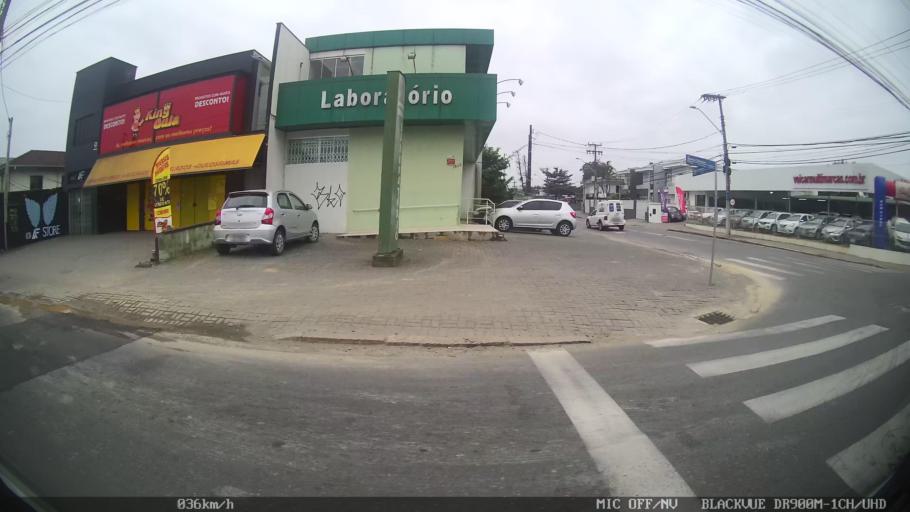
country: BR
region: Santa Catarina
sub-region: Joinville
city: Joinville
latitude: -26.3378
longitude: -48.8475
